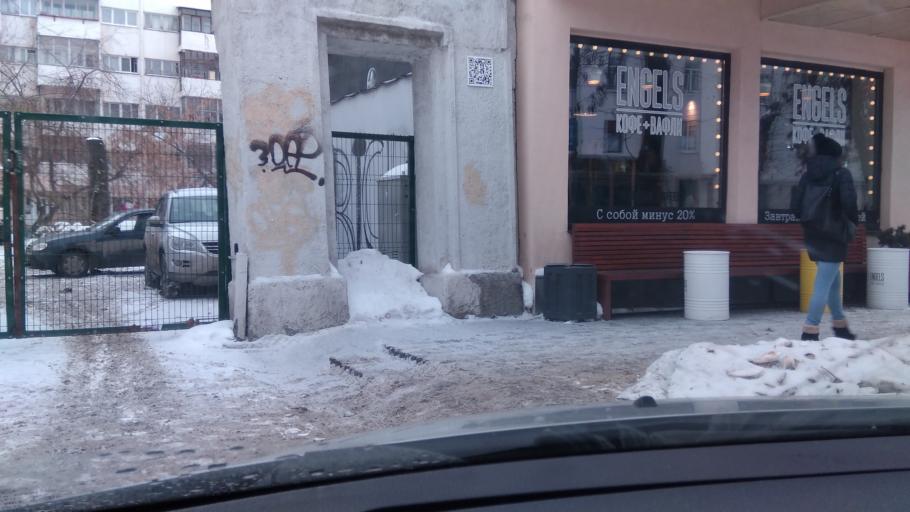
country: RU
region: Sverdlovsk
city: Yekaterinburg
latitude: 56.8335
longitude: 60.5921
